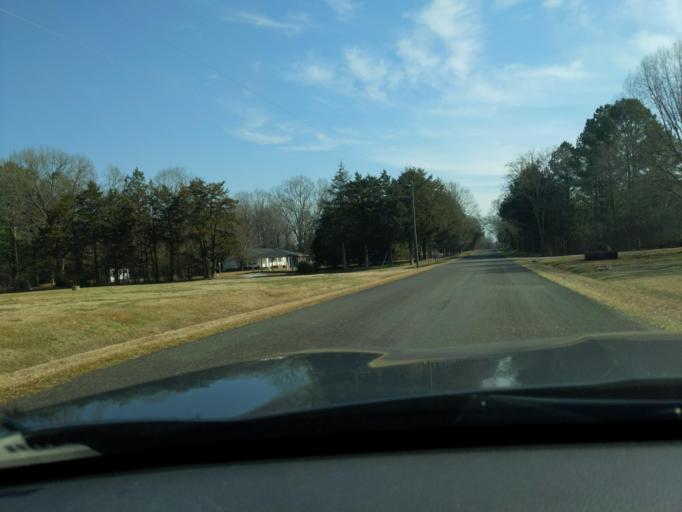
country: US
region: South Carolina
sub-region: Abbeville County
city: Calhoun Falls
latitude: 34.0927
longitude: -82.5587
